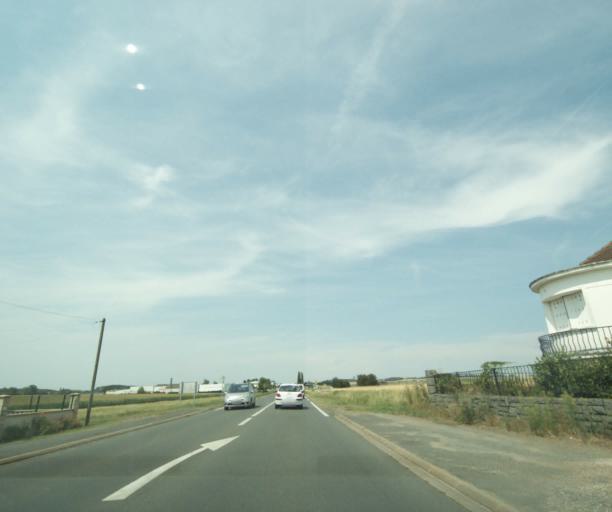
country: FR
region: Poitou-Charentes
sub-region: Departement de la Vienne
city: Dange-Saint-Romain
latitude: 46.9431
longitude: 0.6073
